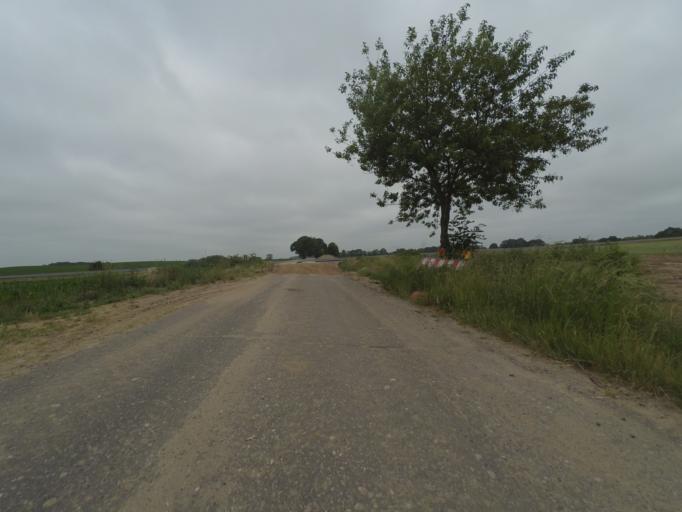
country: DE
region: Mecklenburg-Vorpommern
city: Plau am See
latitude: 53.4672
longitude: 12.2527
